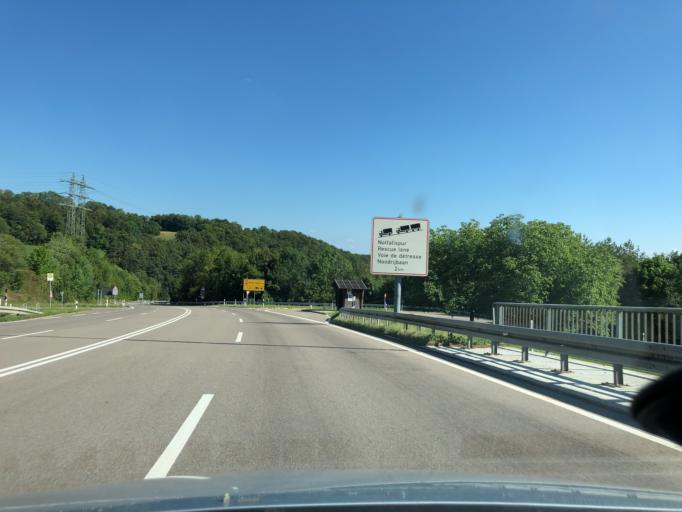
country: DE
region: Baden-Wuerttemberg
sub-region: Freiburg Region
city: Dogern
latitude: 47.6427
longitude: 8.1790
